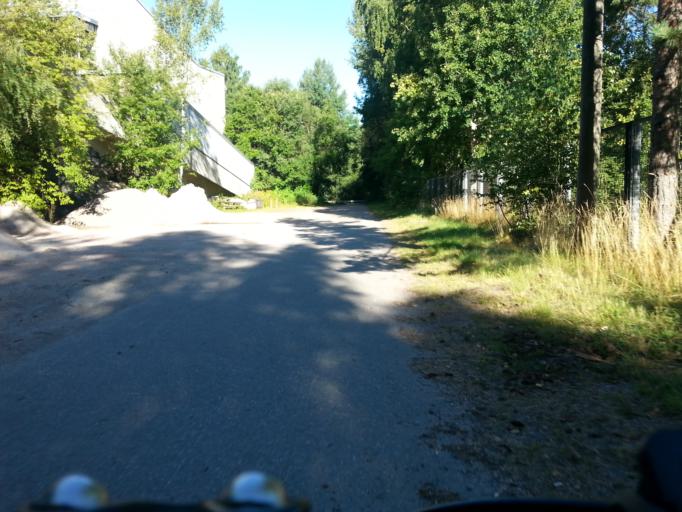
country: FI
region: Uusimaa
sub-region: Helsinki
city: Teekkarikylae
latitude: 60.2241
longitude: 24.8692
